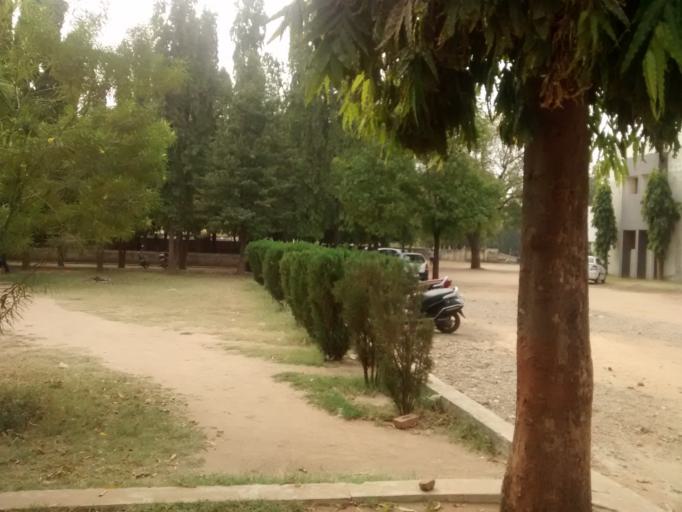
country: IN
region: Gujarat
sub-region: Gandhinagar
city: Dahegam
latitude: 23.1604
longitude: 72.8039
